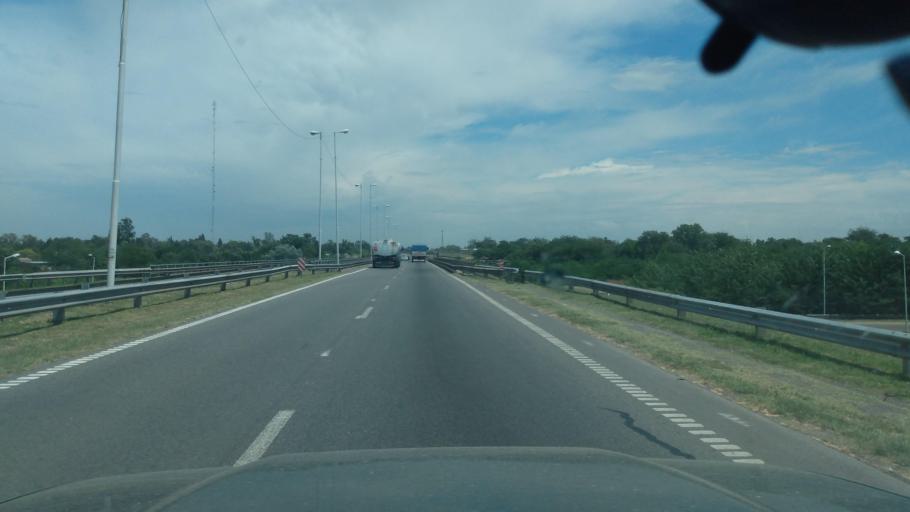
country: AR
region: Buenos Aires
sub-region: Partido de Lujan
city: Lujan
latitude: -34.5492
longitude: -59.1146
